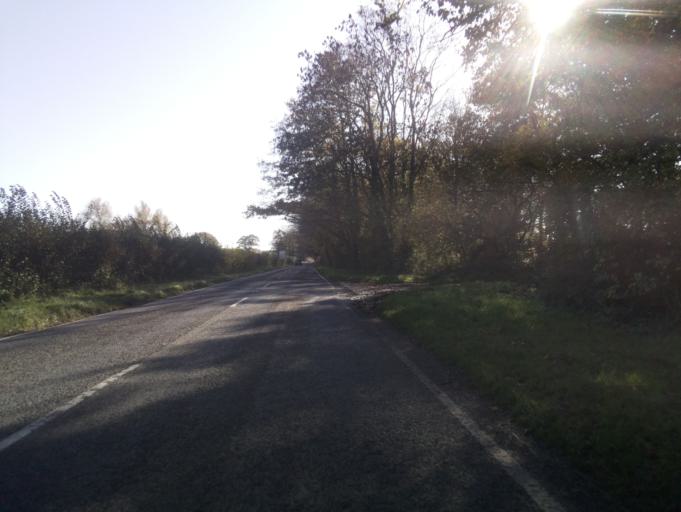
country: GB
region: England
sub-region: Dorset
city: Sherborne
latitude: 50.8816
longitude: -2.4857
